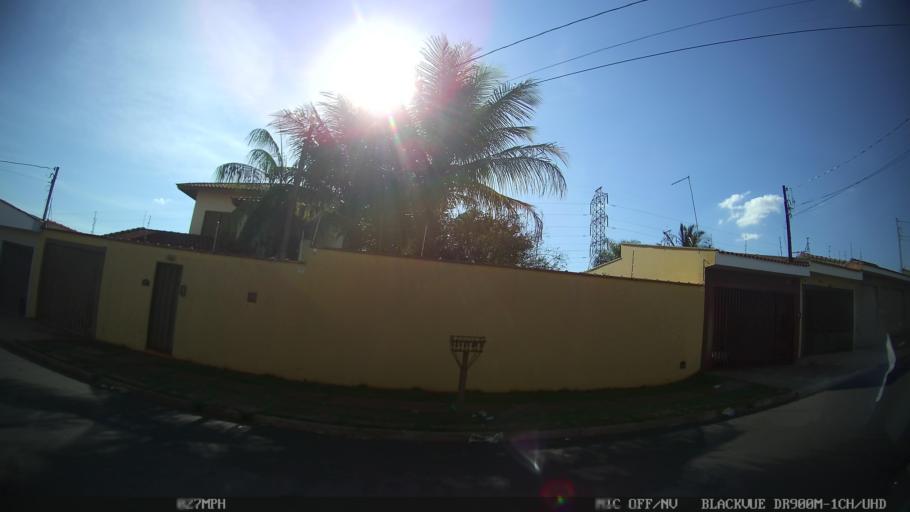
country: BR
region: Sao Paulo
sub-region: Ribeirao Preto
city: Ribeirao Preto
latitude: -21.1743
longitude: -47.7731
